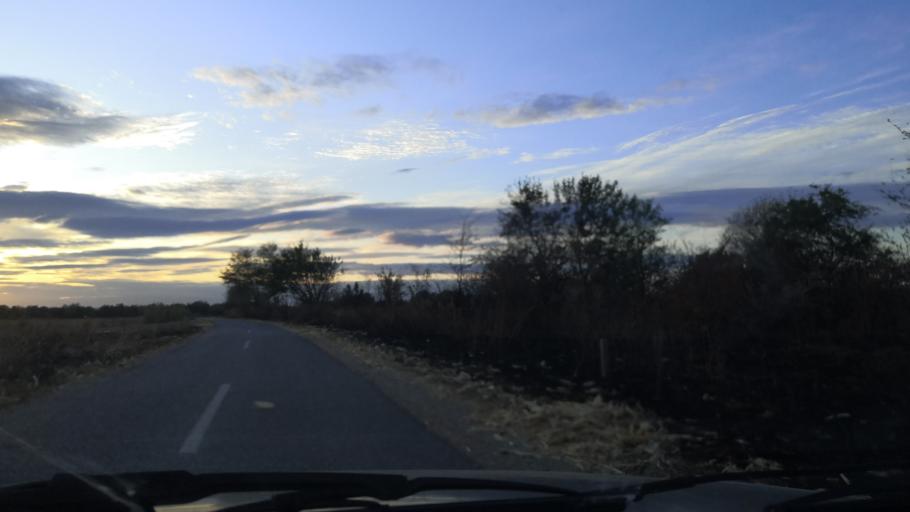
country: RO
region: Mehedinti
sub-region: Comuna Gruia
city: Izvoarele
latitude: 44.2793
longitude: 22.6506
